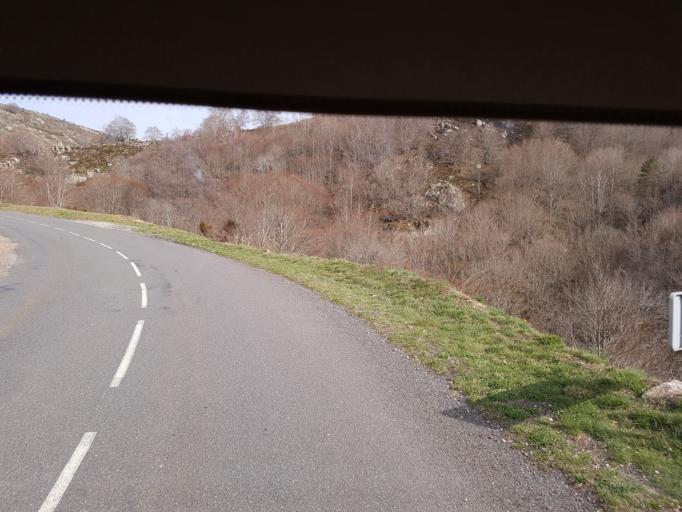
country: FR
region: Languedoc-Roussillon
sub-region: Departement de la Lozere
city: Florac
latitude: 44.3575
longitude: 3.7697
